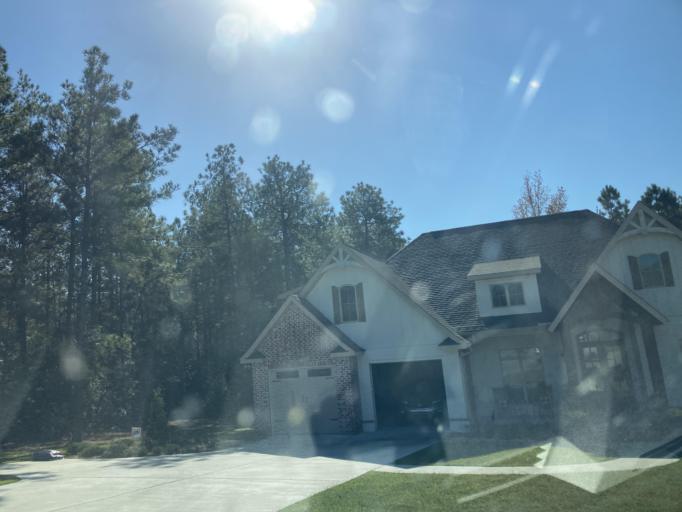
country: US
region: Mississippi
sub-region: Lamar County
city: Sumrall
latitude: 31.3305
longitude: -89.4849
